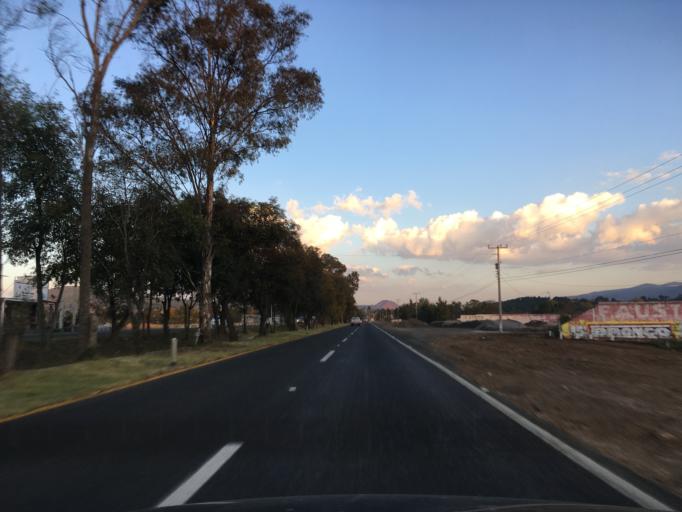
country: MX
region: Michoacan
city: Cuanajo
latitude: 19.5369
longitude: -101.5211
